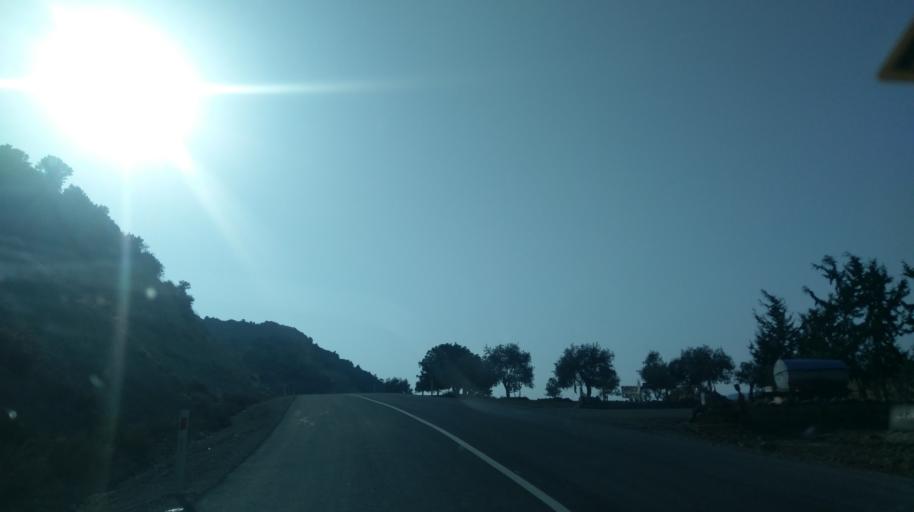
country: CY
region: Ammochostos
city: Rizokarpaso
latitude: 35.5239
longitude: 34.2963
